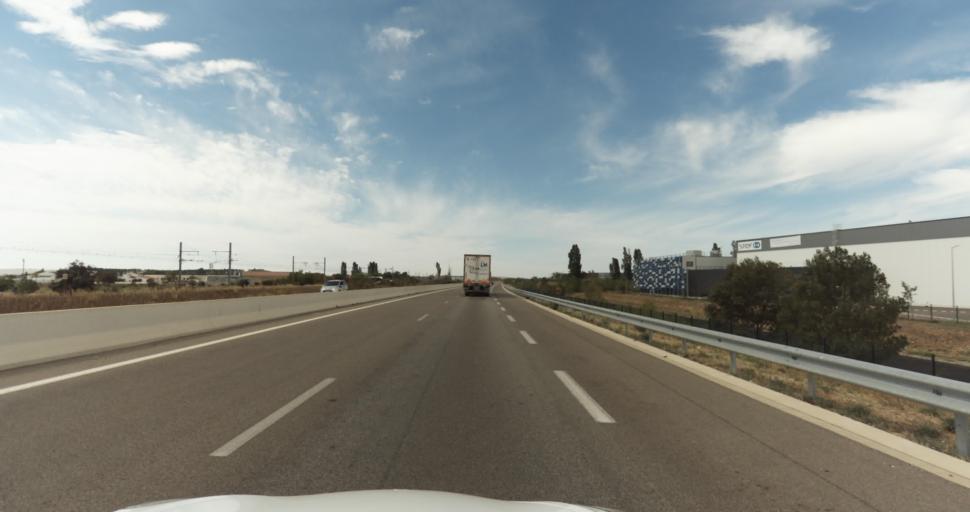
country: FR
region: Provence-Alpes-Cote d'Azur
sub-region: Departement des Bouches-du-Rhone
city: Miramas
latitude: 43.6031
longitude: 5.0026
